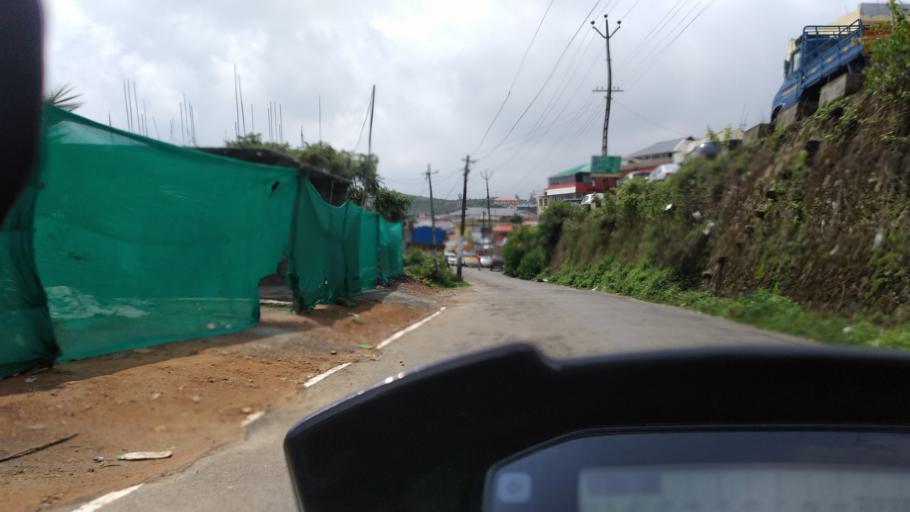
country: IN
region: Kerala
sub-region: Kottayam
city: Erattupetta
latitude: 9.6292
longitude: 76.9793
